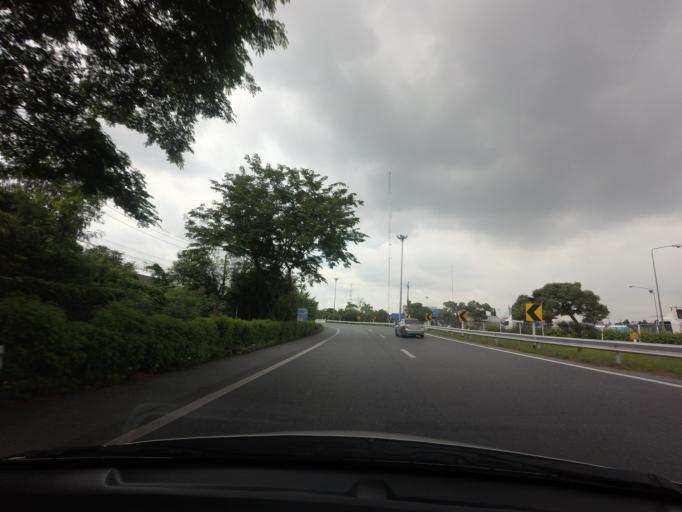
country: TH
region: Bangkok
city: Saphan Sung
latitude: 13.7794
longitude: 100.6857
